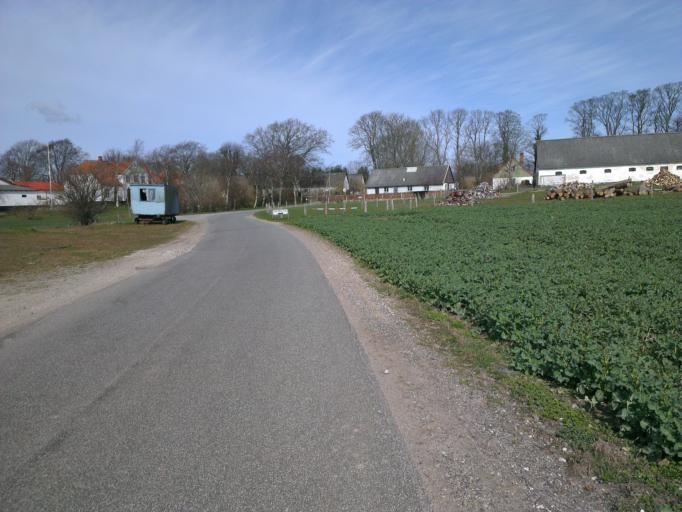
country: DK
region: Capital Region
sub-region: Frederikssund Kommune
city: Frederikssund
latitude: 55.8332
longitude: 12.1187
